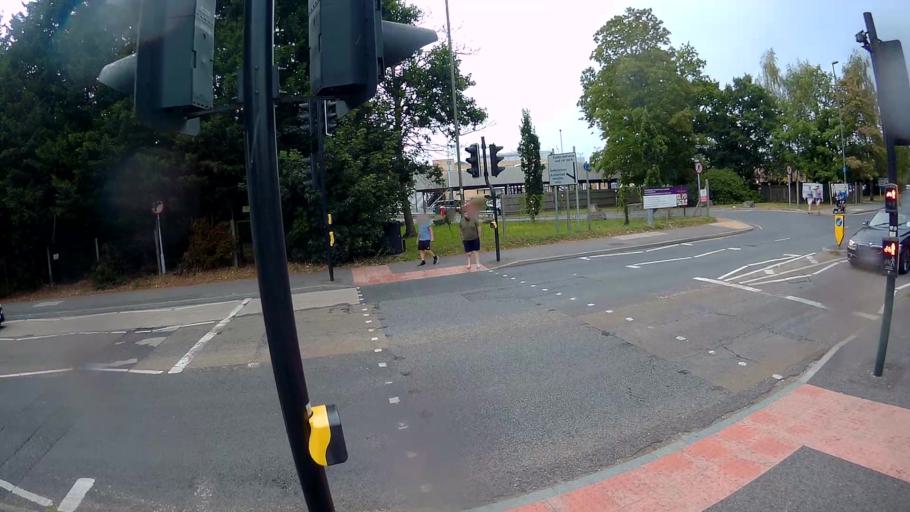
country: GB
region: England
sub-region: Surrey
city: Frimley
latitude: 51.3173
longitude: -0.7410
